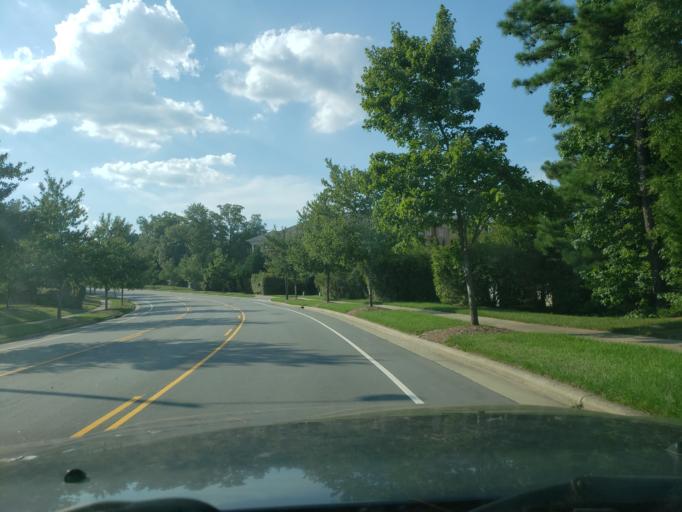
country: US
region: North Carolina
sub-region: Orange County
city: Chapel Hill
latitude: 35.9048
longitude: -79.0068
